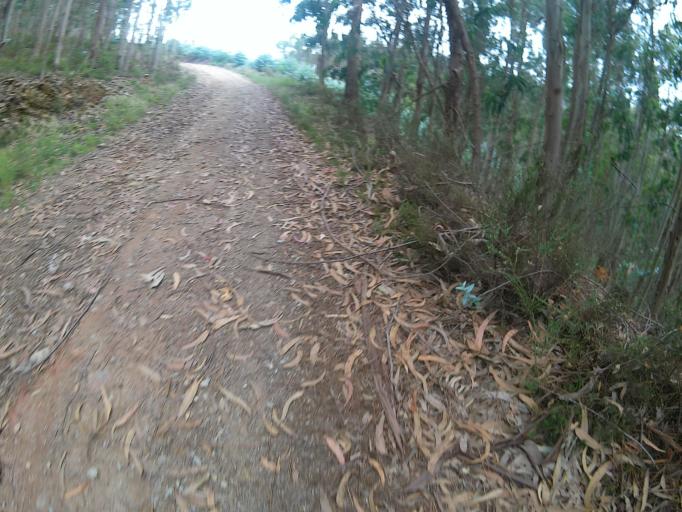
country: PT
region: Aveiro
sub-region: Albergaria-A-Velha
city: Branca
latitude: 40.7609
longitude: -8.4306
